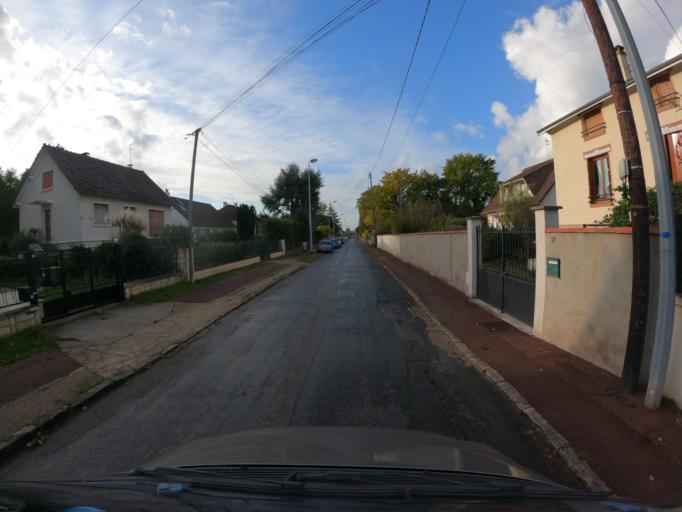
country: FR
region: Ile-de-France
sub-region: Departement de Seine-et-Marne
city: Brou-sur-Chantereine
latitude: 48.8813
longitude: 2.6360
